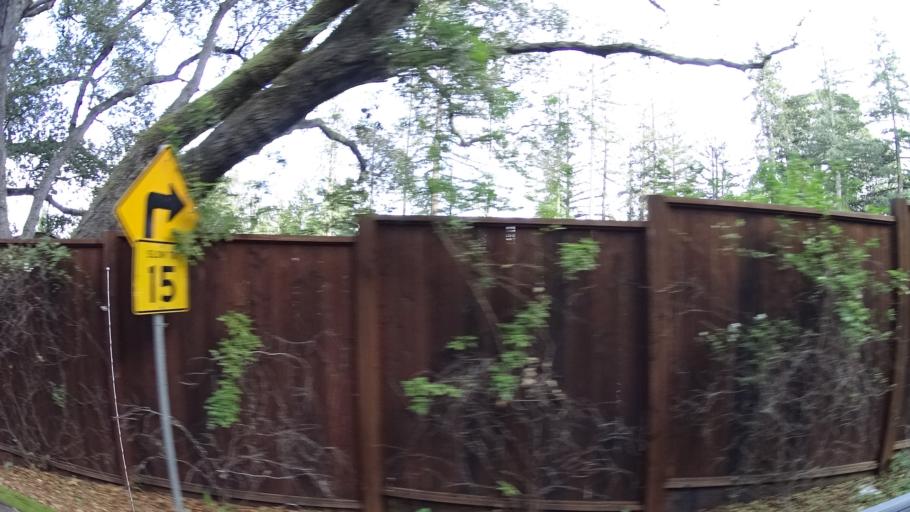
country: US
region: California
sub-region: San Mateo County
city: Hillsborough
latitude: 37.5630
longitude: -122.3647
